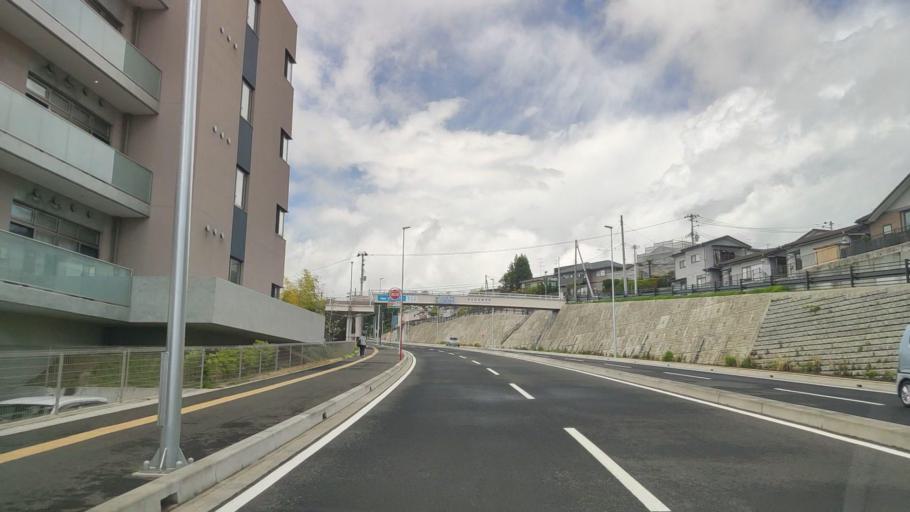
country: JP
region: Miyagi
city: Sendai
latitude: 38.2353
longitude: 140.8521
